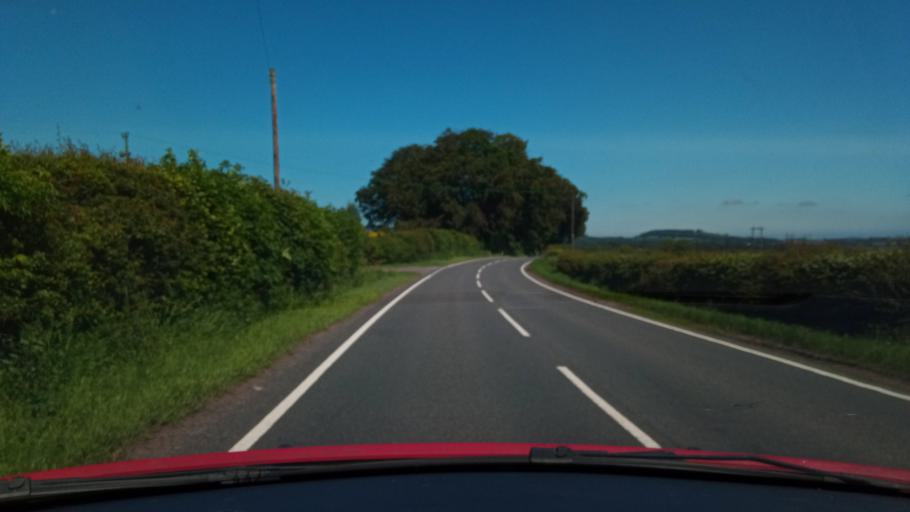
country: GB
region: Scotland
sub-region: The Scottish Borders
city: Duns
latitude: 55.7550
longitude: -2.4021
